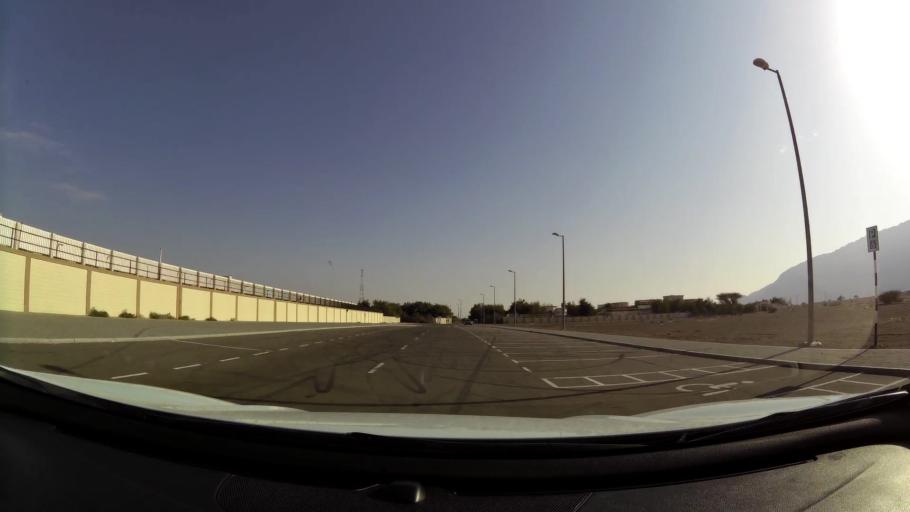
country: AE
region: Abu Dhabi
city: Al Ain
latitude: 24.0397
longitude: 55.8399
